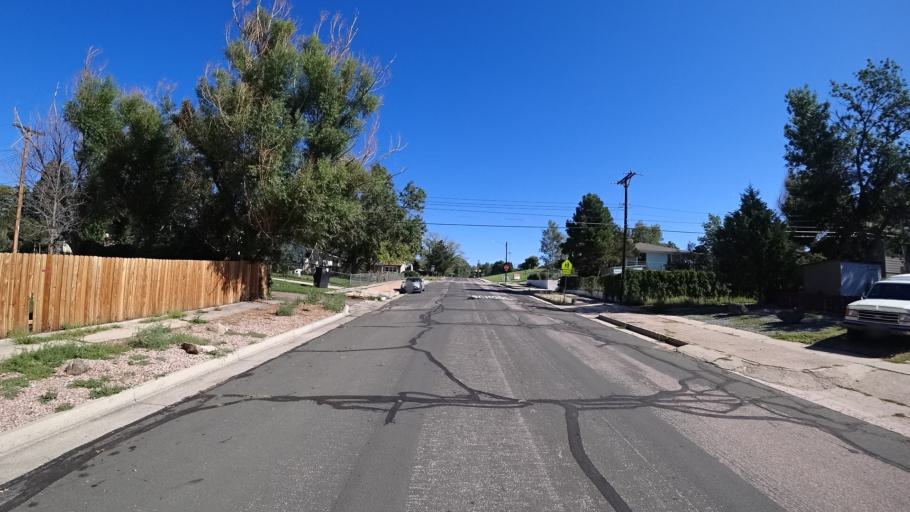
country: US
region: Colorado
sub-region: El Paso County
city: Colorado Springs
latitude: 38.8563
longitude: -104.7827
